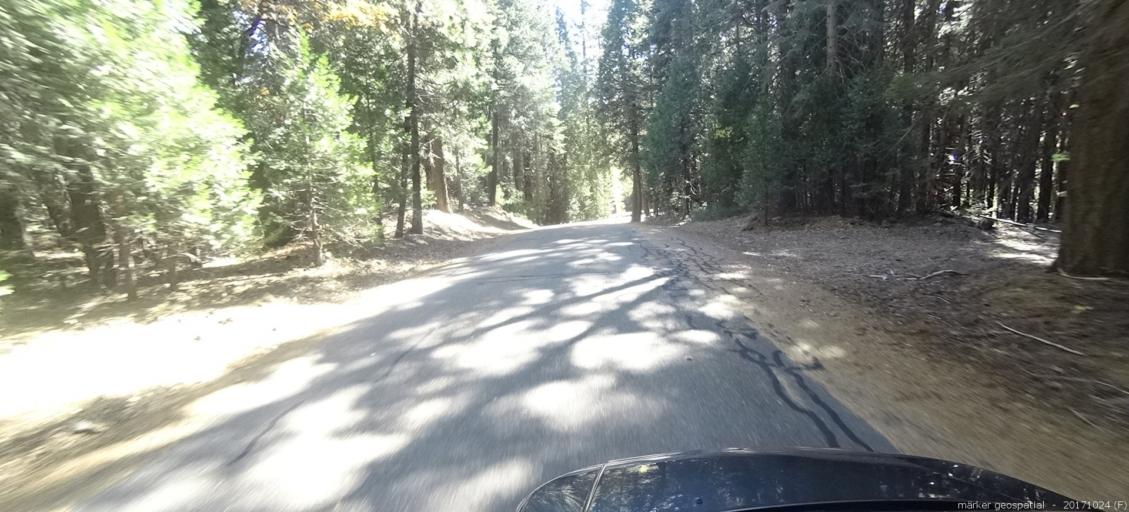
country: US
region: California
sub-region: Shasta County
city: Shingletown
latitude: 40.5011
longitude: -121.6597
